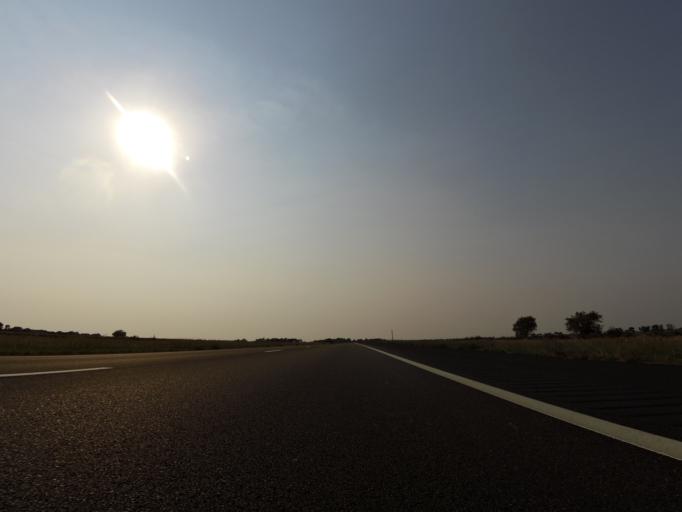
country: US
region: Kansas
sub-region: Reno County
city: Haven
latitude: 37.8778
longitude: -97.7056
